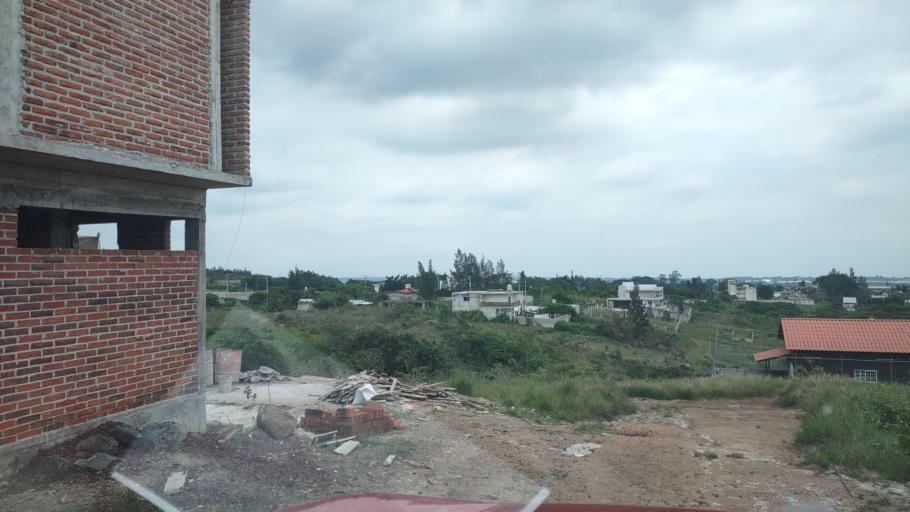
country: MX
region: Veracruz
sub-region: Emiliano Zapata
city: Dos Rios
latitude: 19.4842
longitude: -96.8262
